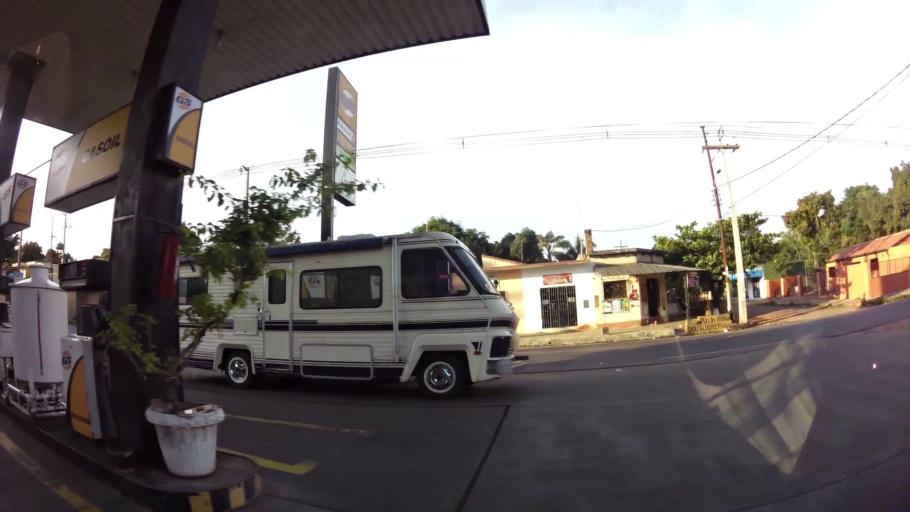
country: PY
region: Central
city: San Lorenzo
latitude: -25.3612
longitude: -57.5048
